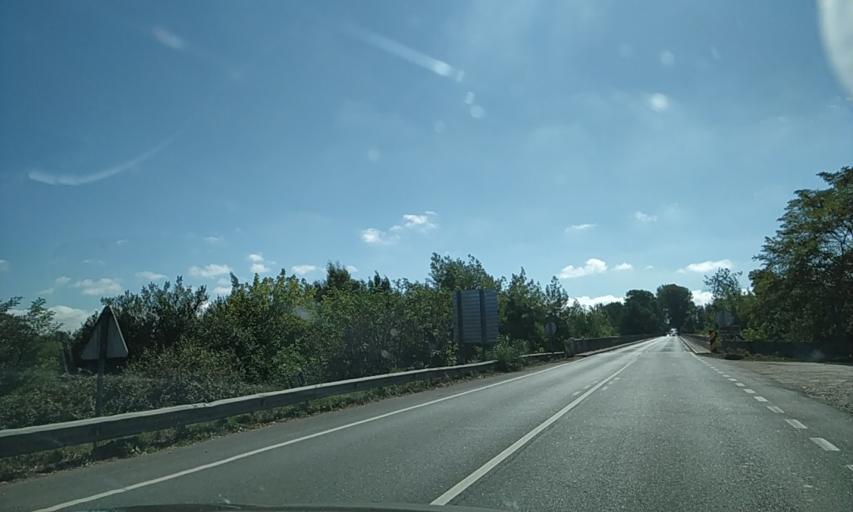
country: PT
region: Aveiro
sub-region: Aveiro
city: Eixo
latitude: 40.6817
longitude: -8.5796
